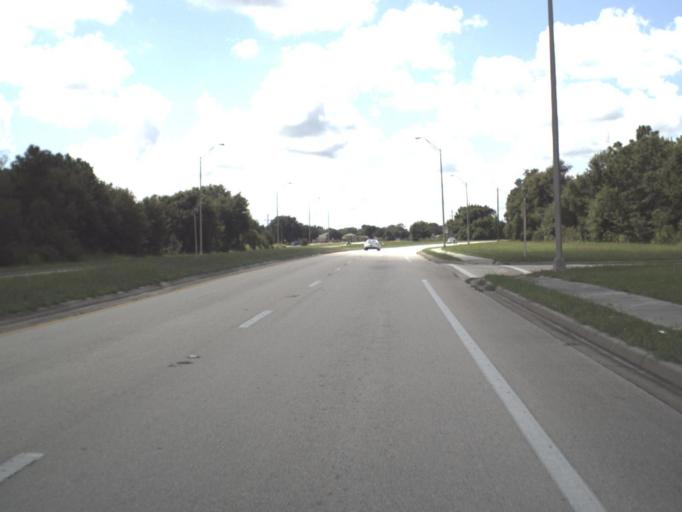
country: US
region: Florida
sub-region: DeSoto County
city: Arcadia
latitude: 27.2346
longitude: -81.8527
